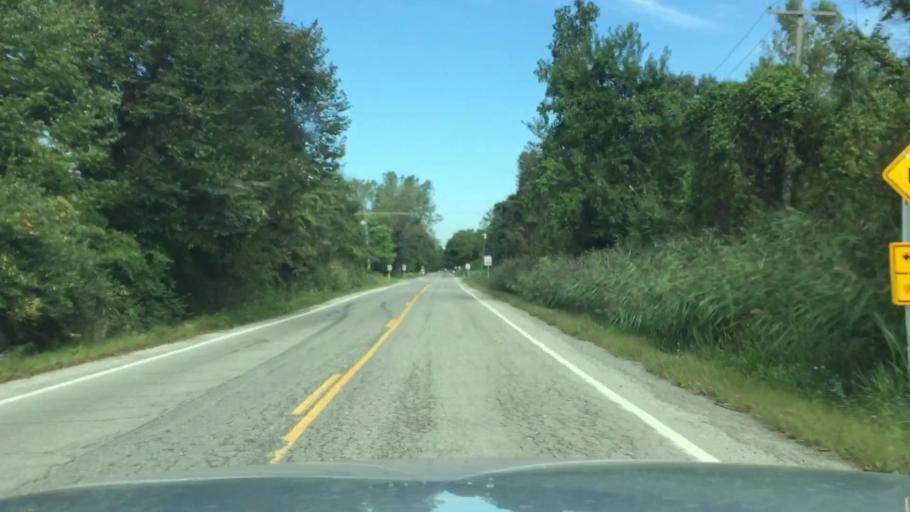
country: US
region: Michigan
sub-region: Wayne County
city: Belleville
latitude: 42.1588
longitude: -83.4614
